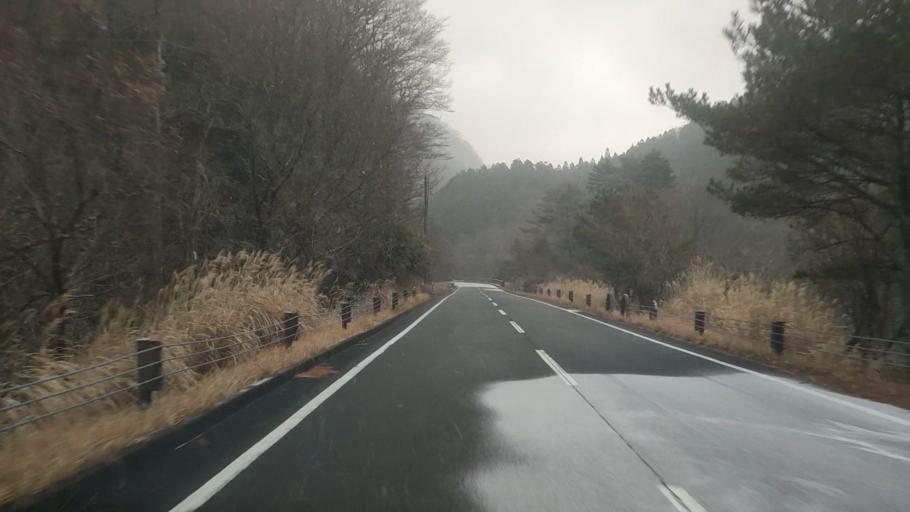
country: JP
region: Kumamoto
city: Matsubase
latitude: 32.5665
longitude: 130.9104
